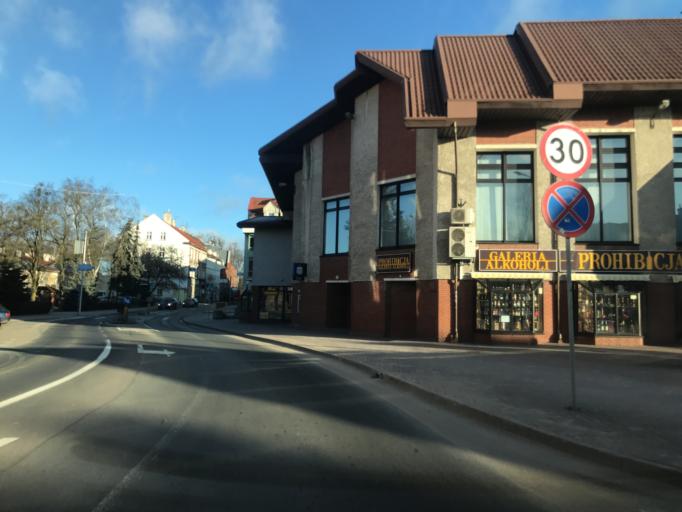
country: PL
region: Warmian-Masurian Voivodeship
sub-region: Powiat ostrodzki
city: Ostroda
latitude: 53.7016
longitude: 19.9610
